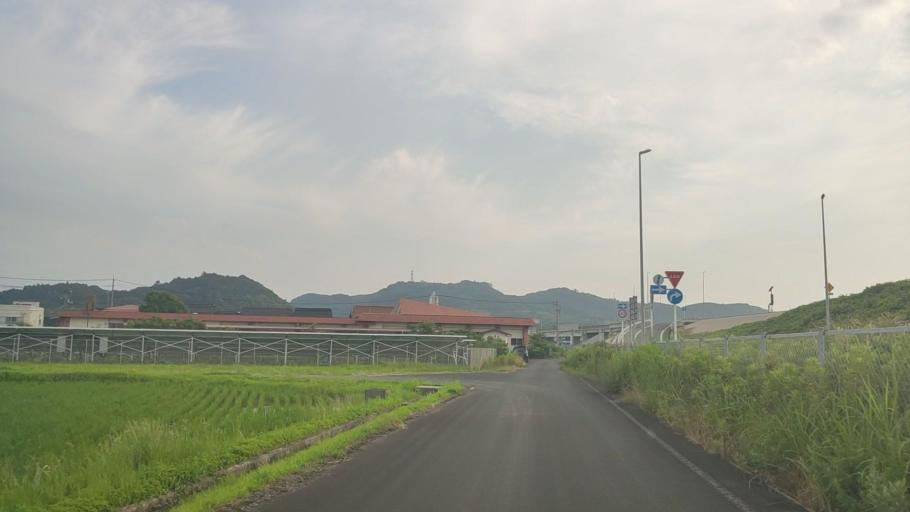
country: JP
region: Tottori
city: Kurayoshi
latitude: 35.4854
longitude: 133.8090
